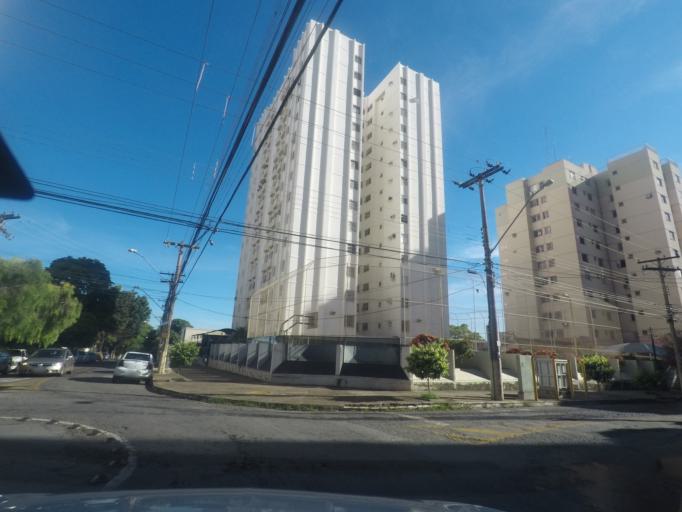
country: BR
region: Goias
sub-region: Goiania
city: Goiania
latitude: -16.6689
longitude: -49.2678
